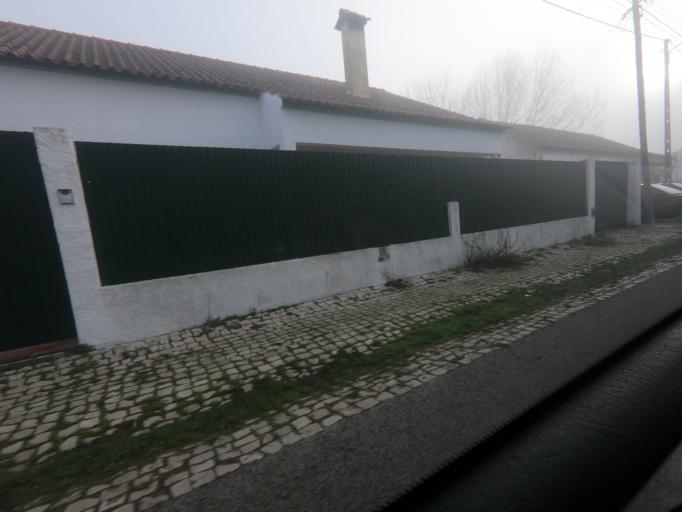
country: PT
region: Setubal
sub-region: Palmela
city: Pinhal Novo
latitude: 38.6104
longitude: -8.8915
